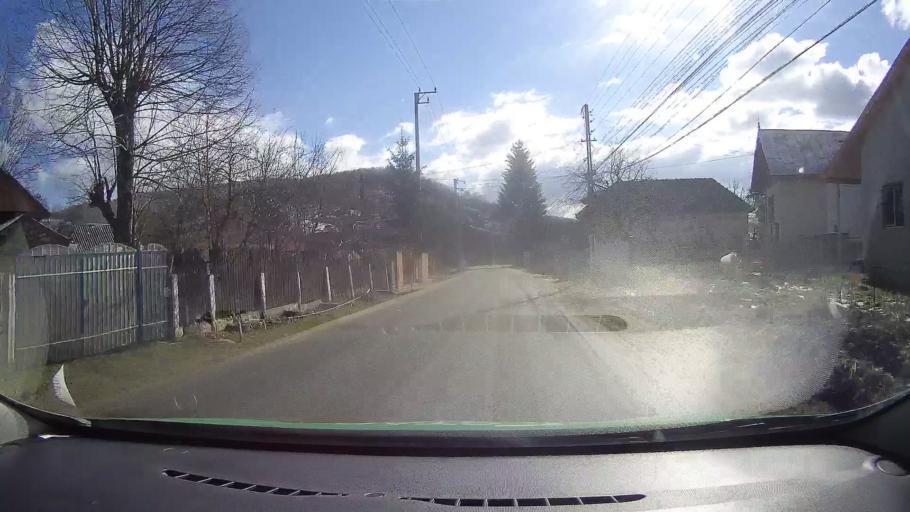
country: RO
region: Dambovita
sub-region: Comuna Runcu
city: Runcu
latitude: 45.1715
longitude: 25.3931
